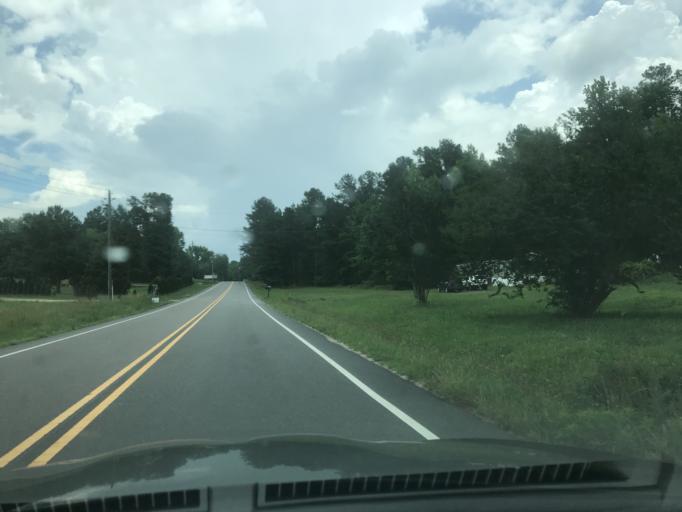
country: US
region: North Carolina
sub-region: Wake County
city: Knightdale
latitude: 35.8361
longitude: -78.4764
